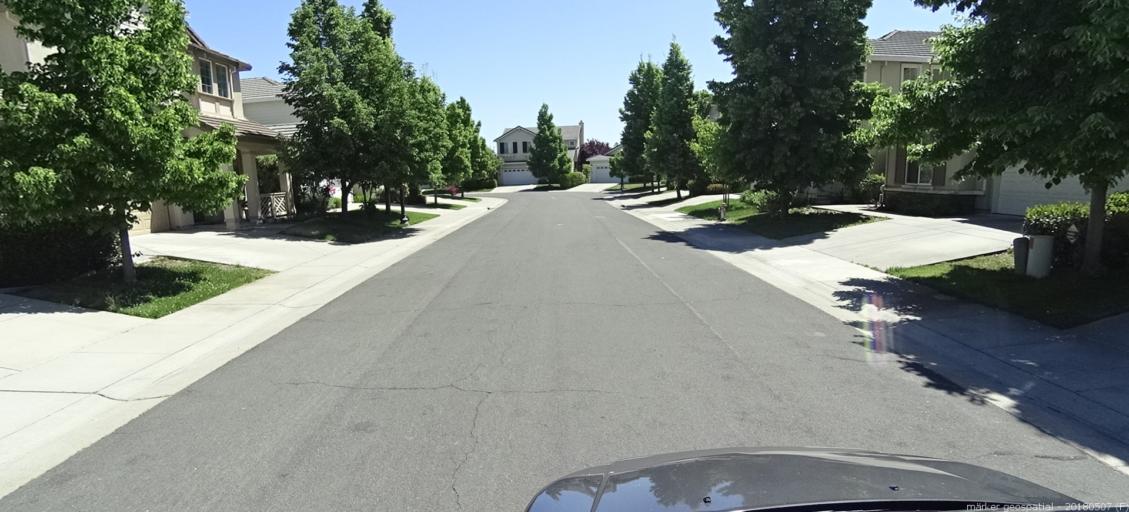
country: US
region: California
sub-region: Sacramento County
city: Elverta
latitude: 38.6755
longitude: -121.5092
